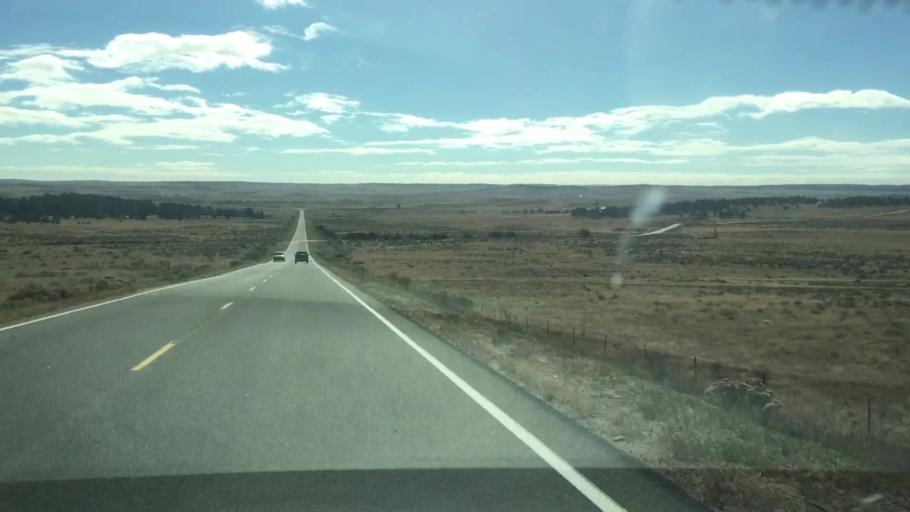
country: US
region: Colorado
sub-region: Elbert County
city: Kiowa
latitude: 39.3109
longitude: -104.3613
